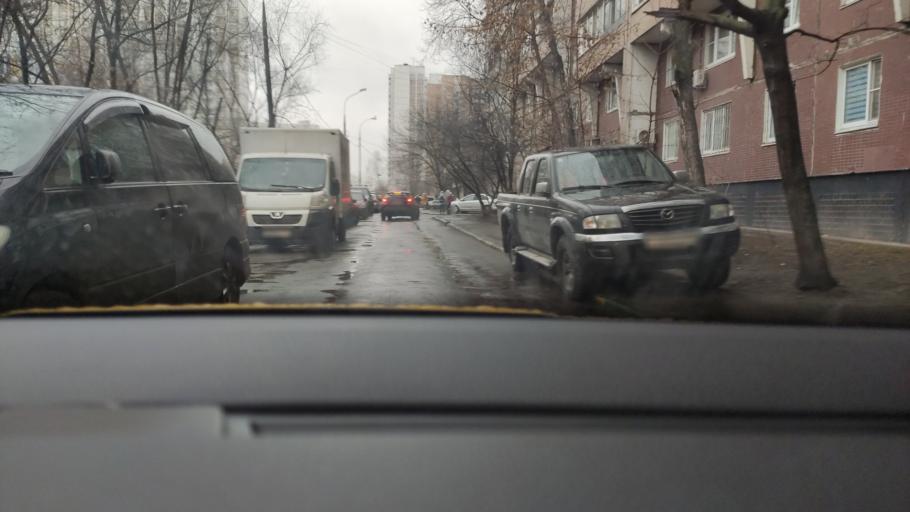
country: RU
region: Moscow
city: Mar'ino
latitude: 55.6511
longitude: 37.7345
